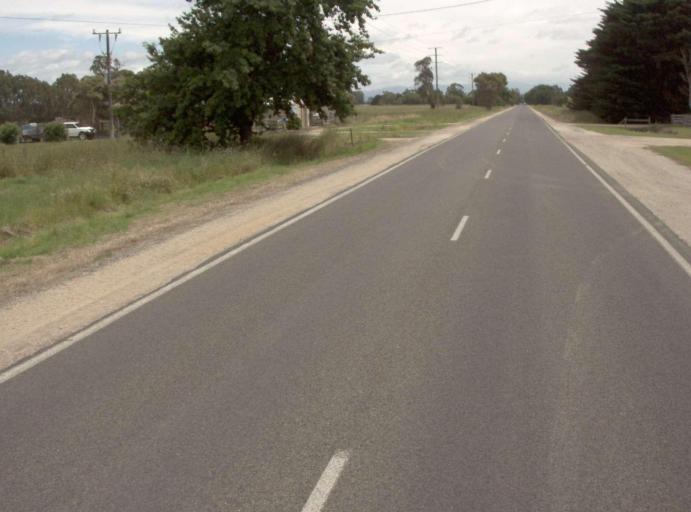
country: AU
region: Victoria
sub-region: Wellington
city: Sale
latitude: -38.0111
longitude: 147.0067
